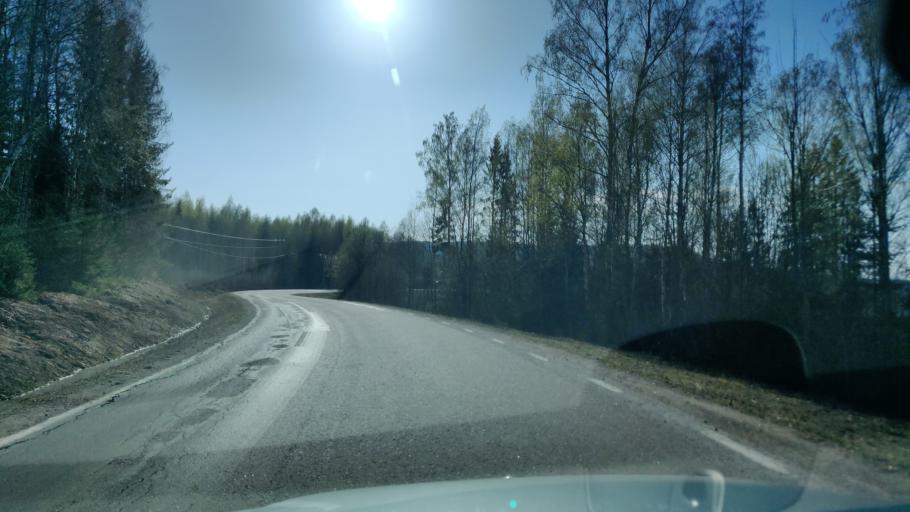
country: SE
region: Vaermland
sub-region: Munkfors Kommun
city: Munkfors
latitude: 59.9707
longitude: 13.4528
